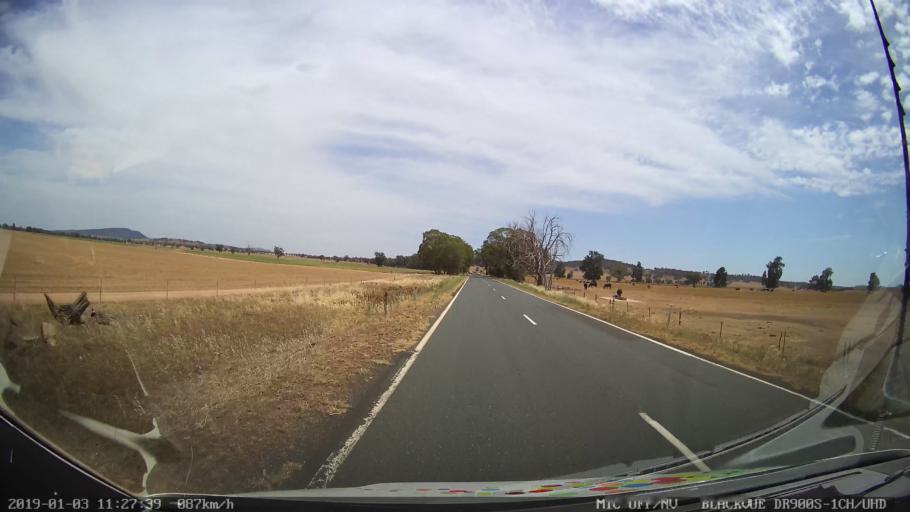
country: AU
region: New South Wales
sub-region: Weddin
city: Grenfell
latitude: -34.0102
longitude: 148.2173
